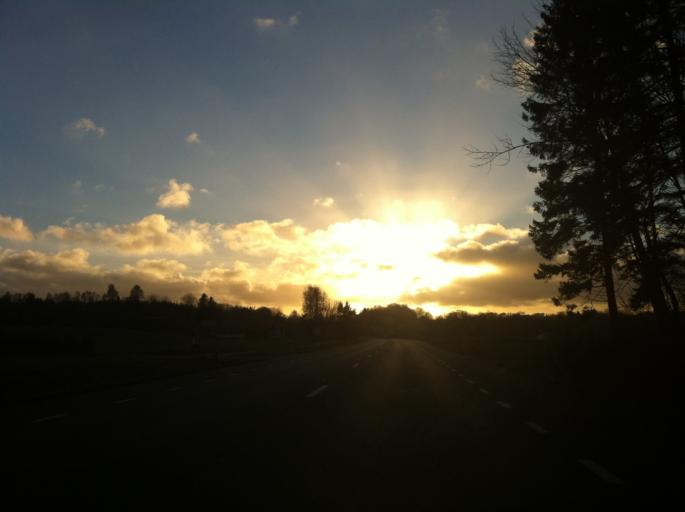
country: SE
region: Skane
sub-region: Hassleholms Kommun
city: Sosdala
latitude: 56.0450
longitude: 13.7084
